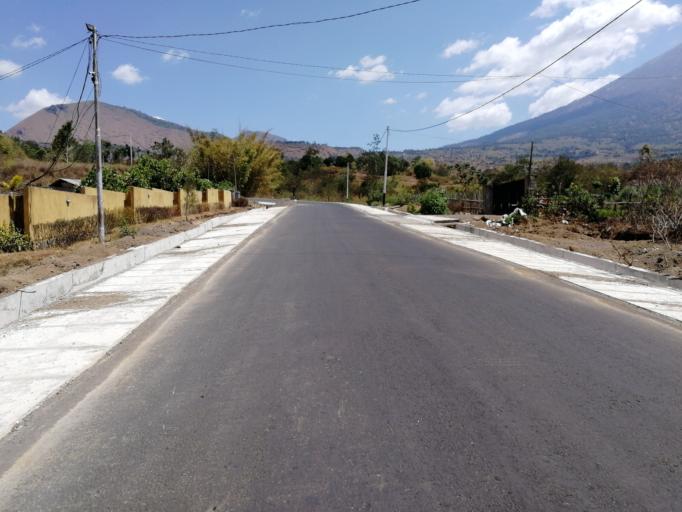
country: ID
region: West Nusa Tenggara
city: Sembalunlawang
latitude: -8.3568
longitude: 116.5139
